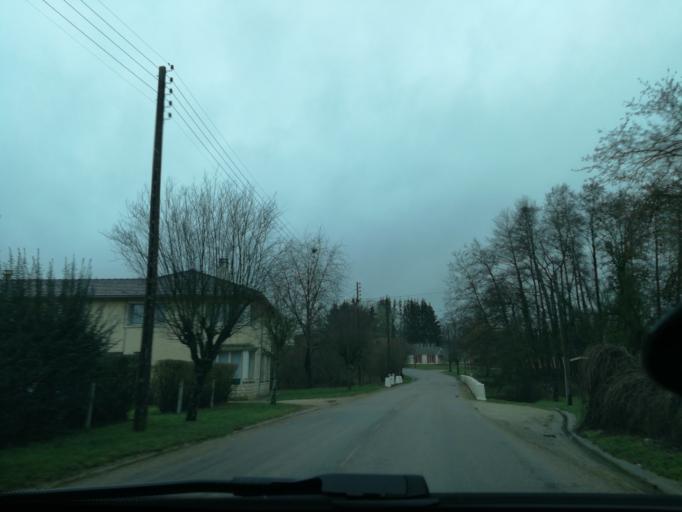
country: FR
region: Lorraine
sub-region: Departement de la Meuse
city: Clermont-en-Argonne
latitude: 48.9993
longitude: 5.0995
